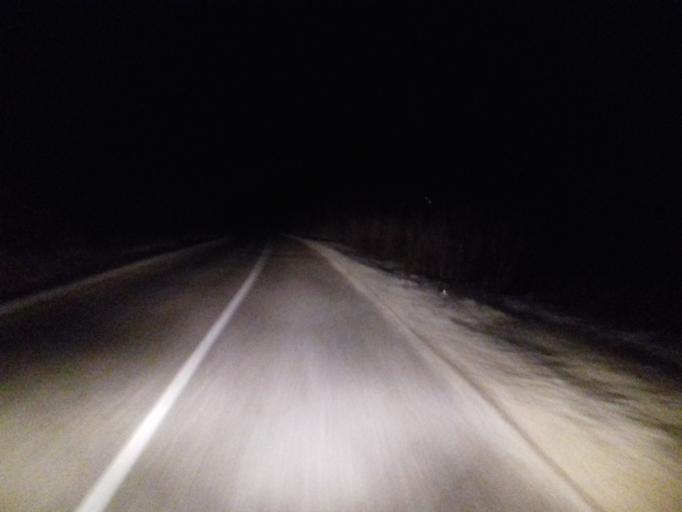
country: BA
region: Federation of Bosnia and Herzegovina
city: Gracanica
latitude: 43.7385
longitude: 18.3281
